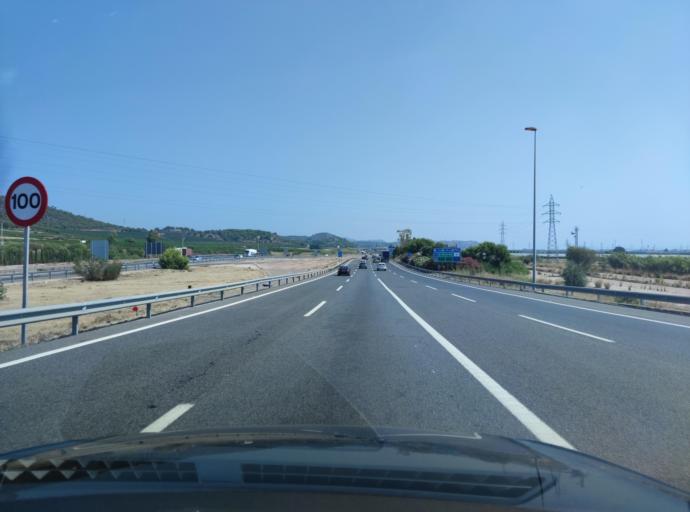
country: ES
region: Valencia
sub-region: Provincia de Valencia
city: Pucol
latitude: 39.6354
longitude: -0.3031
